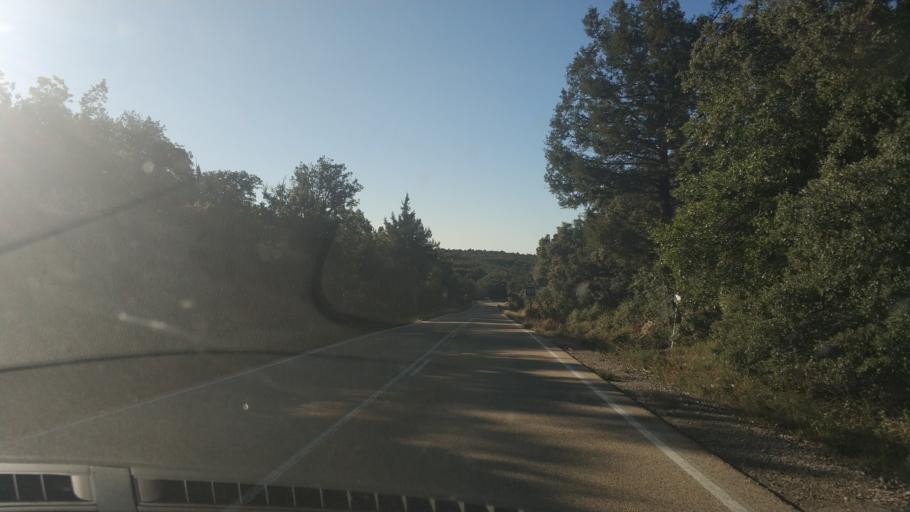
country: ES
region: Castille and Leon
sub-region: Provincia de Soria
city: Montejo de Tiermes
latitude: 41.4152
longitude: -3.2031
